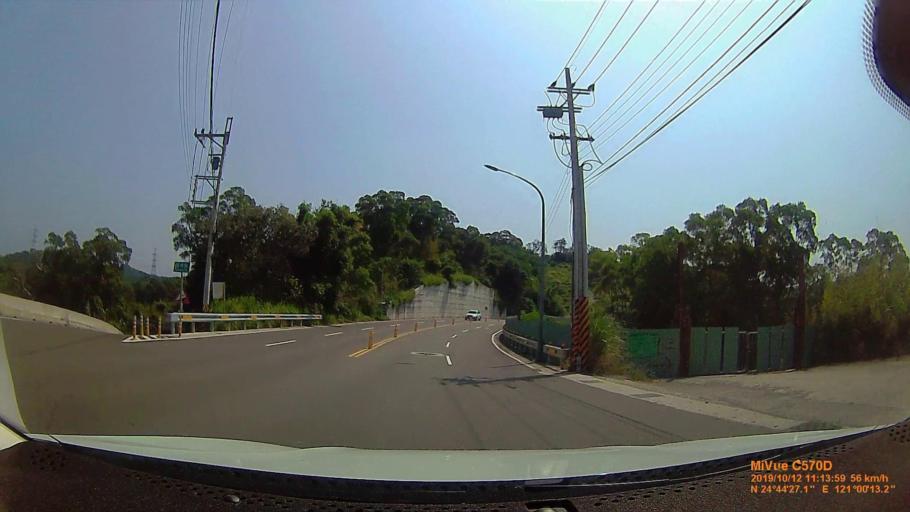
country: TW
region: Taiwan
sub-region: Hsinchu
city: Hsinchu
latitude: 24.7407
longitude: 121.0038
